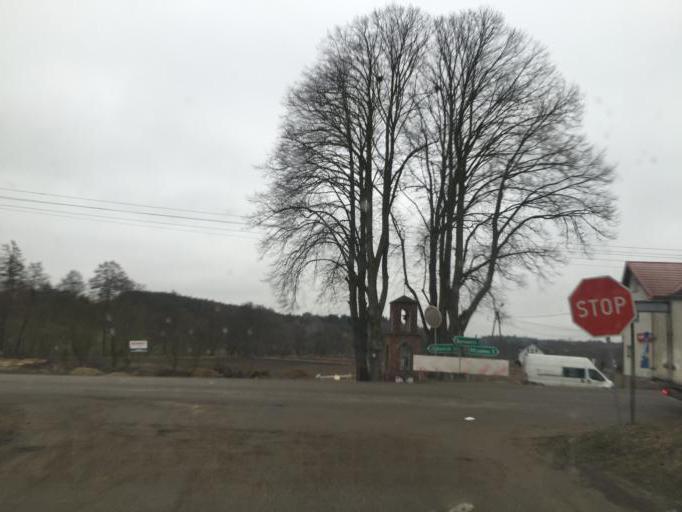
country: PL
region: Pomeranian Voivodeship
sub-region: Powiat kartuski
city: Banino
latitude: 54.3859
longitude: 18.4269
